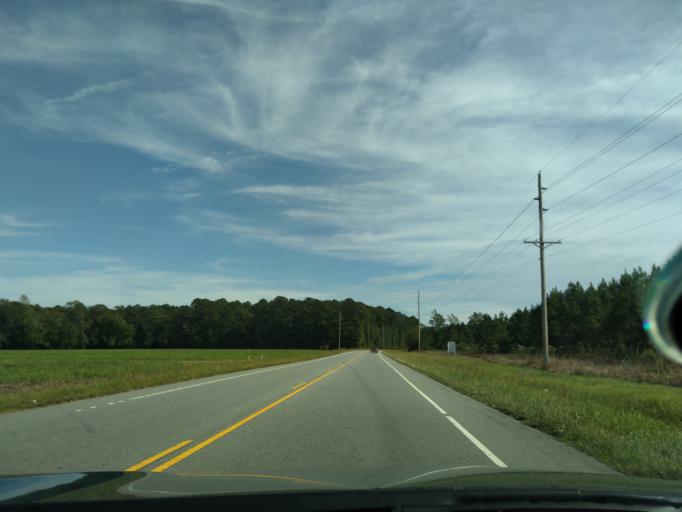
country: US
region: North Carolina
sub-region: Beaufort County
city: River Road
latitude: 35.5215
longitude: -76.9305
